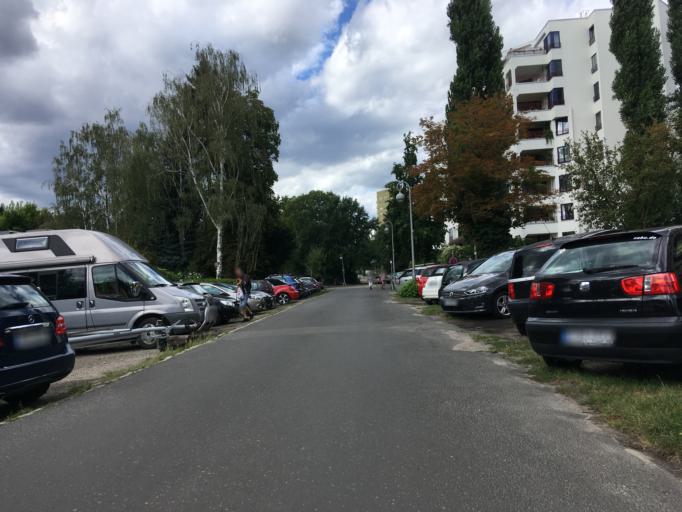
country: DE
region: Berlin
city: Wilhelmstadt
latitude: 52.5121
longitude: 13.1958
